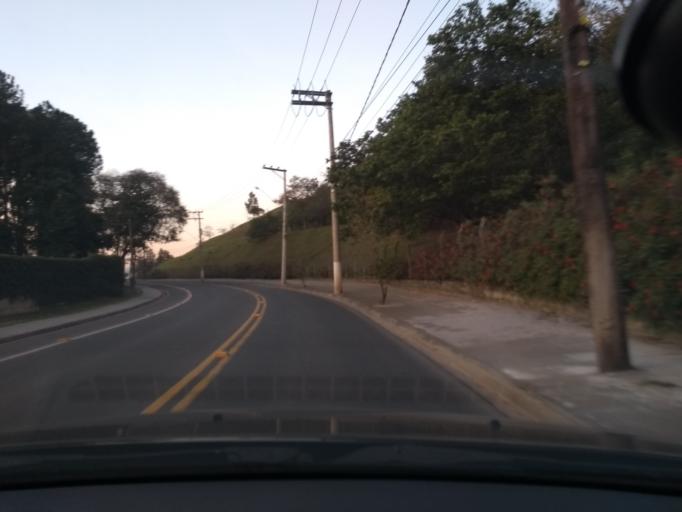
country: BR
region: Sao Paulo
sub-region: Itupeva
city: Itupeva
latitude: -23.1451
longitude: -47.0431
